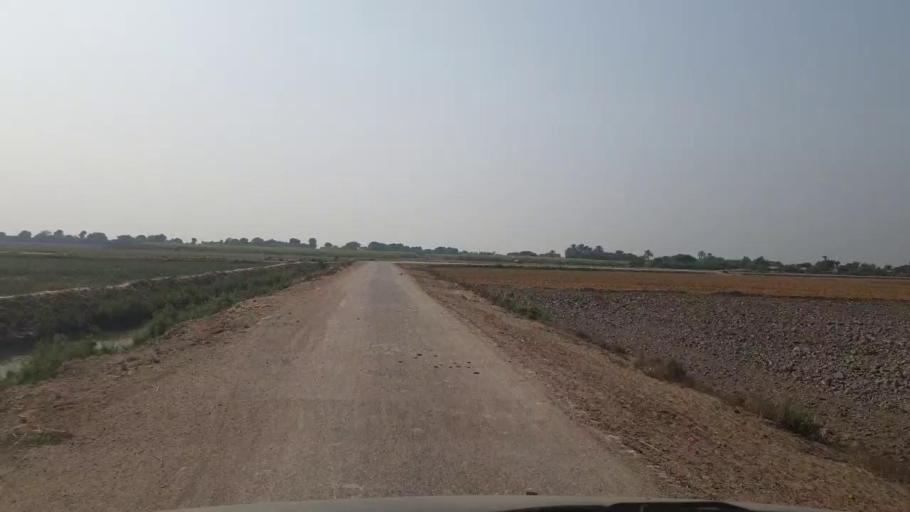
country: PK
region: Sindh
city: Bulri
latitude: 25.0325
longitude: 68.3855
